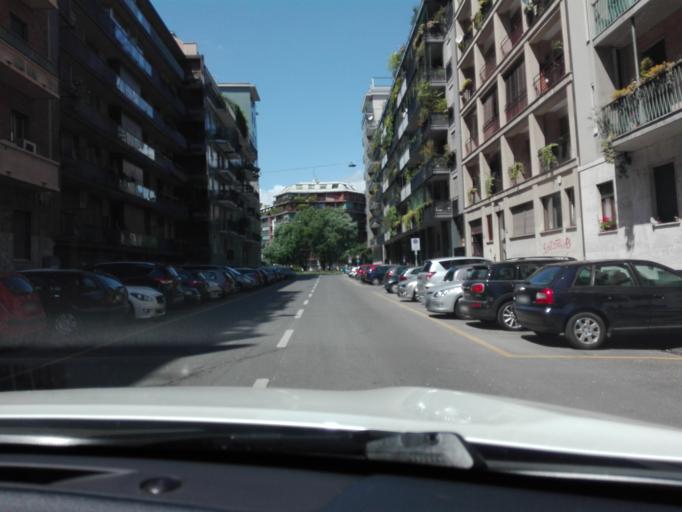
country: IT
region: Lombardy
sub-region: Citta metropolitana di Milano
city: Milano
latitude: 45.4569
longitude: 9.1570
